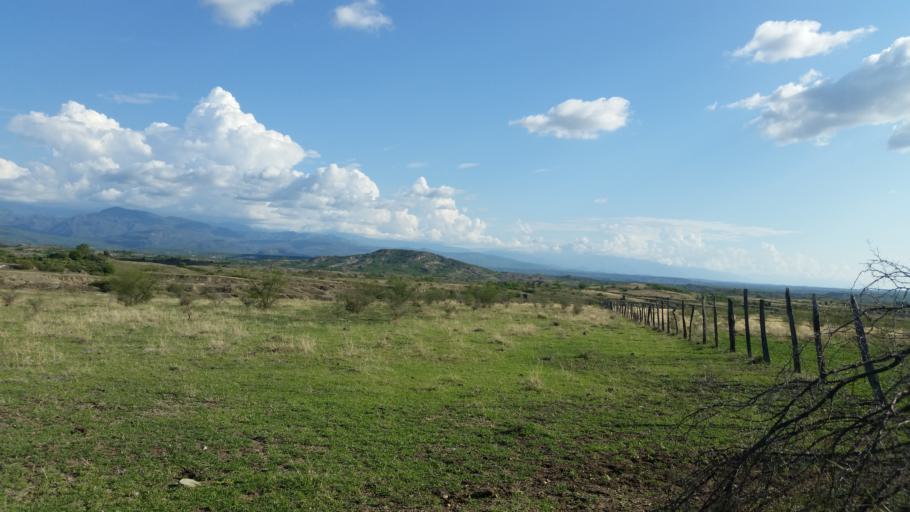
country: CO
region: Huila
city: Baraya
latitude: 3.2371
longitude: -75.1077
